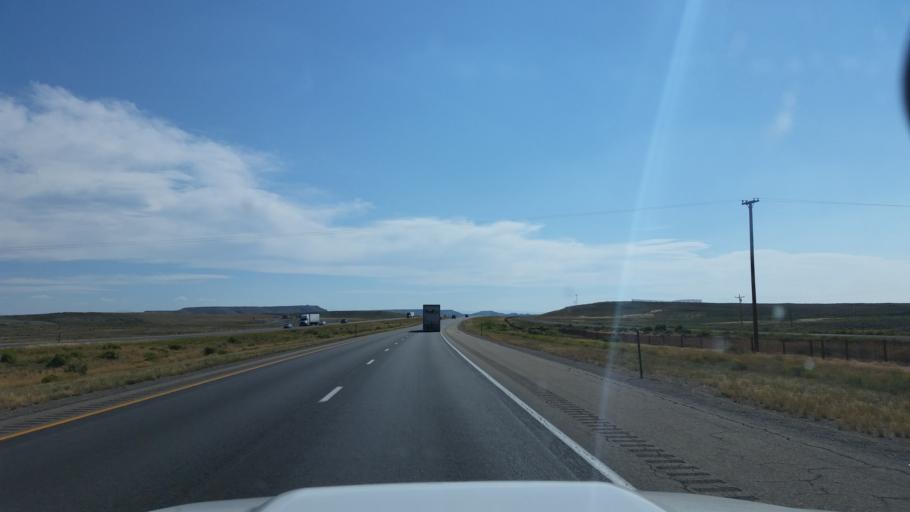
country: US
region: Wyoming
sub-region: Uinta County
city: Lyman
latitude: 41.4724
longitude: -110.0374
